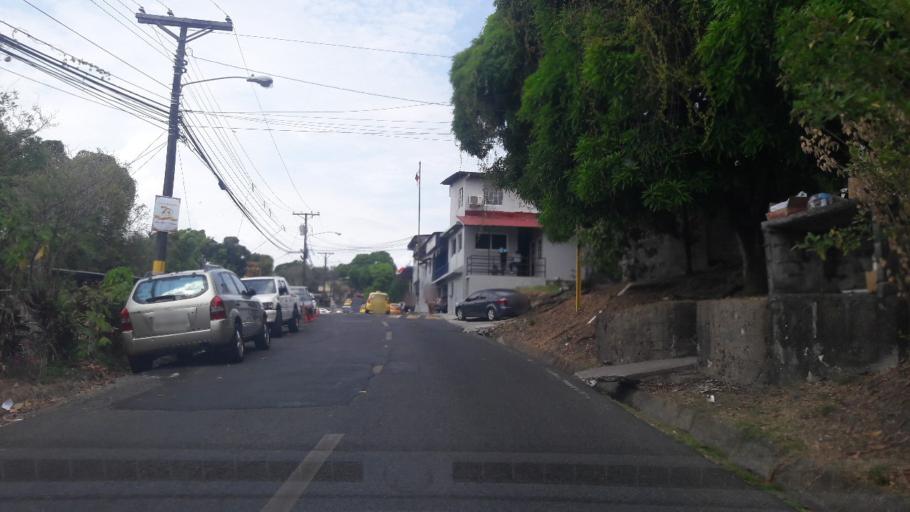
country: PA
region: Panama
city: Alcalde Diaz
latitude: 9.1182
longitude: -79.5549
